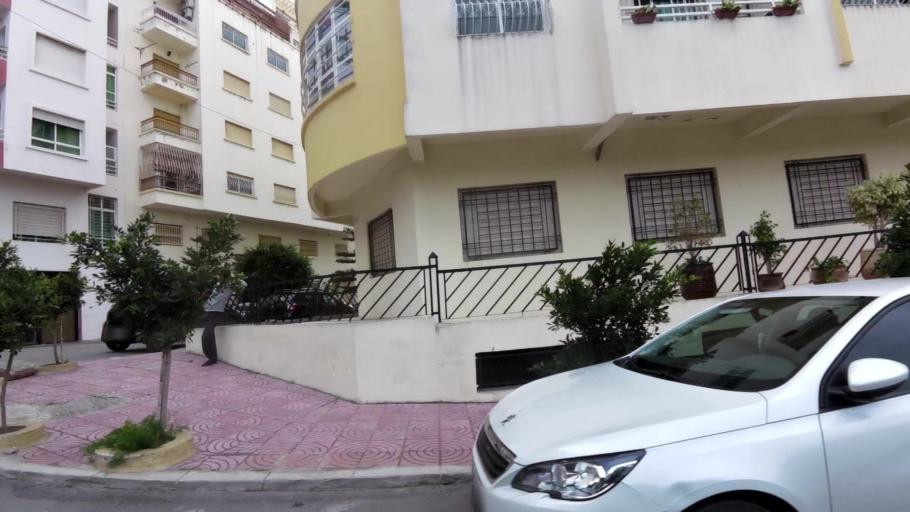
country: MA
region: Tanger-Tetouan
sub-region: Tanger-Assilah
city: Tangier
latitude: 35.7761
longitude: -5.8216
